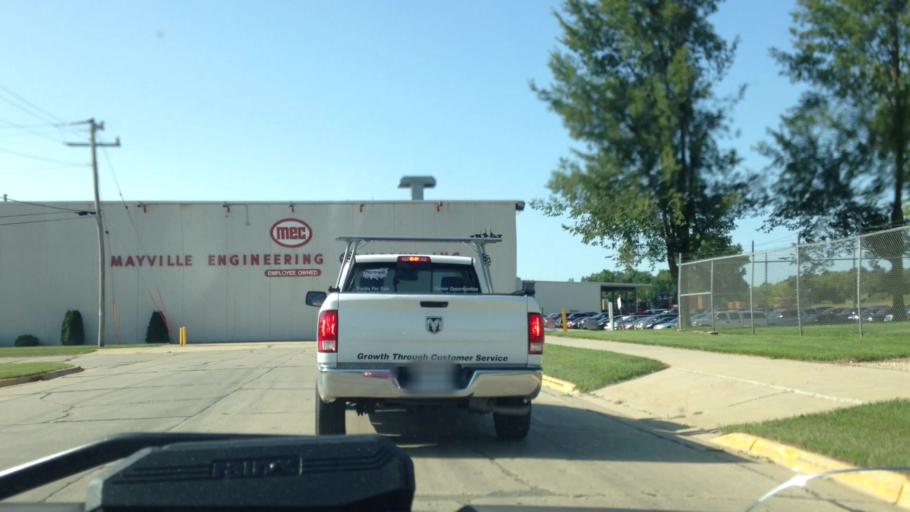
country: US
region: Wisconsin
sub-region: Dodge County
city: Mayville
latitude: 43.4872
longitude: -88.5563
